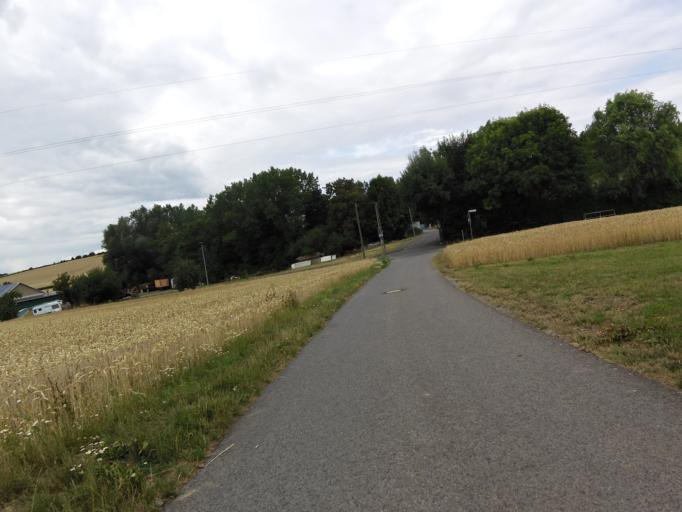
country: DE
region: Bavaria
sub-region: Regierungsbezirk Unterfranken
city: Estenfeld
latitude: 49.8247
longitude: 9.9795
